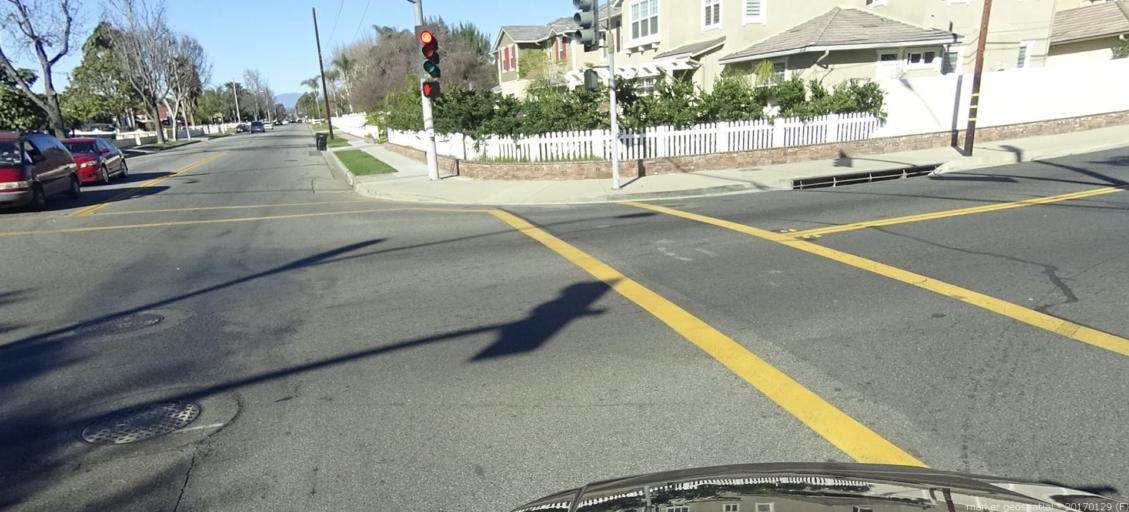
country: US
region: California
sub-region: Orange County
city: Stanton
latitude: 33.8249
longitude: -117.9676
